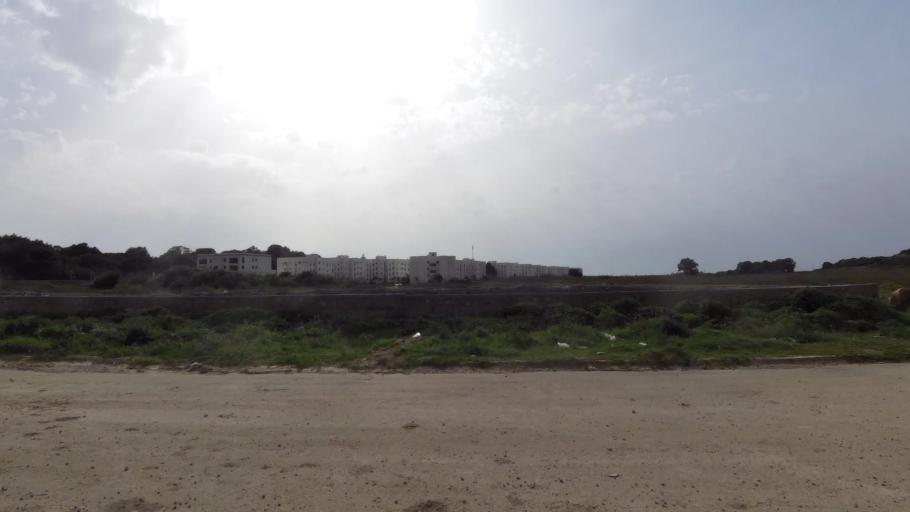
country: MA
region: Tanger-Tetouan
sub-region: Tanger-Assilah
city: Boukhalef
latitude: 35.6844
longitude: -5.9289
